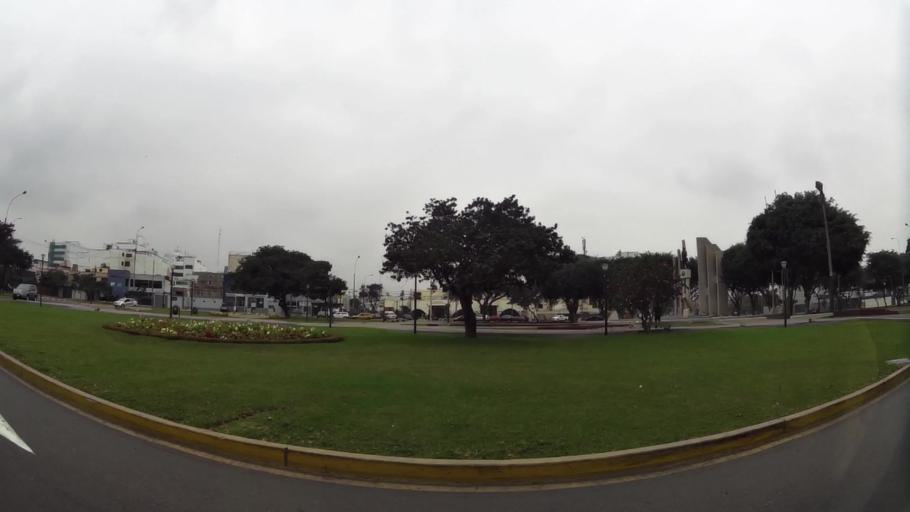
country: PE
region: Lima
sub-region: Lima
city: San Luis
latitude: -12.0982
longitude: -77.0128
